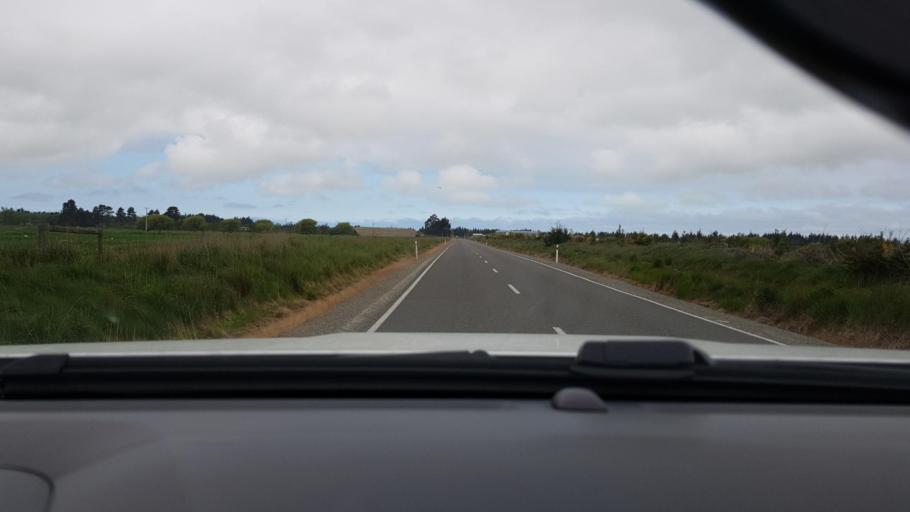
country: NZ
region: Otago
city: Oamaru
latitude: -44.9642
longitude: 171.0640
